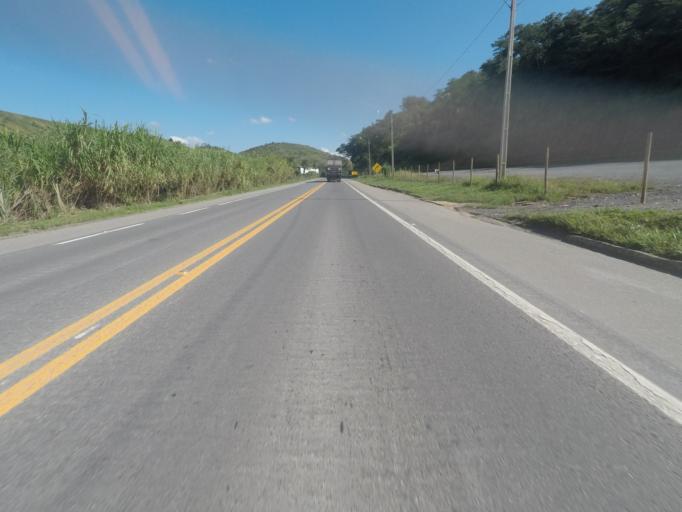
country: BR
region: Espirito Santo
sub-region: Mimoso Do Sul
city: Mimoso do Sul
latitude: -21.1167
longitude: -41.2676
